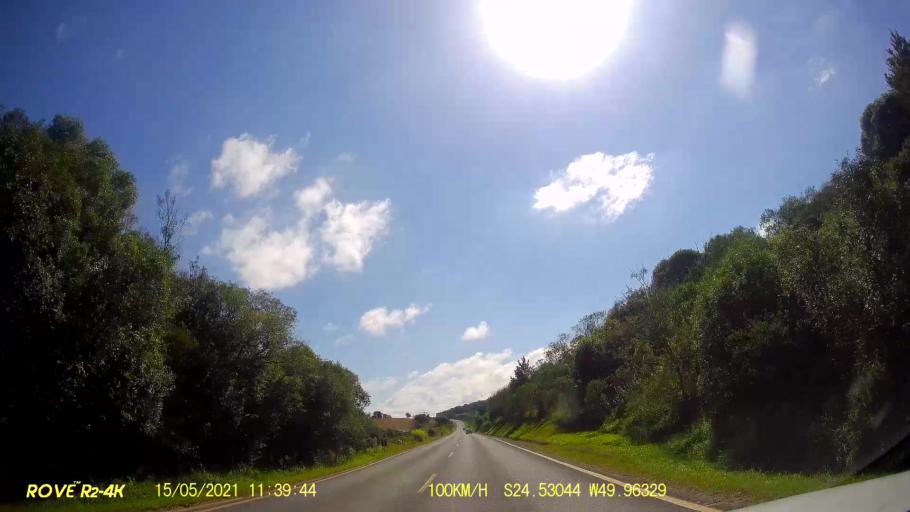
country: BR
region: Parana
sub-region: Pirai Do Sul
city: Pirai do Sul
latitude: -24.5306
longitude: -49.9633
